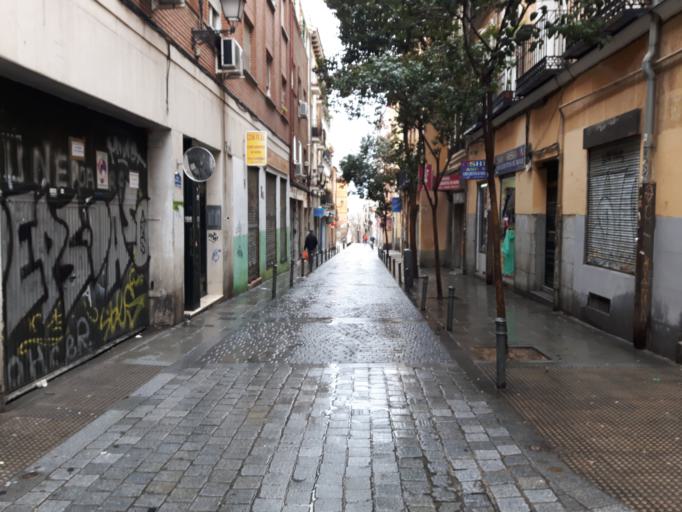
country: ES
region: Madrid
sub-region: Provincia de Madrid
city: Madrid
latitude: 40.4103
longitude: -3.7045
